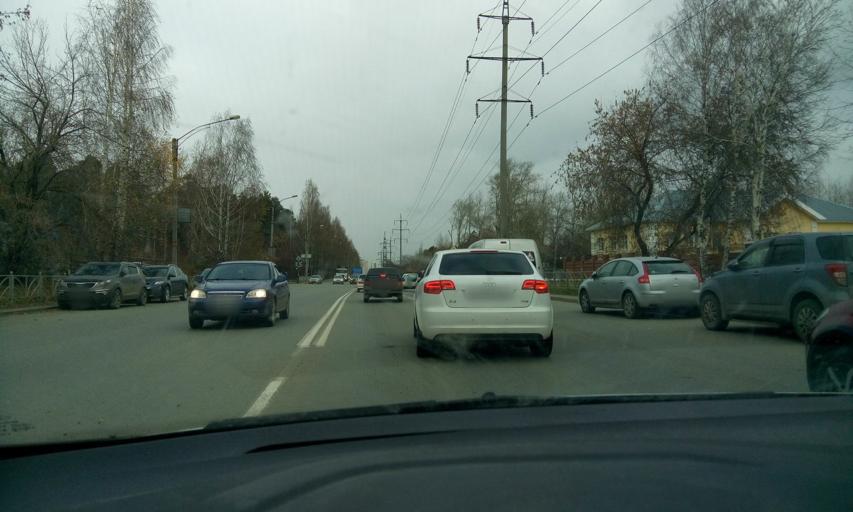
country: RU
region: Sverdlovsk
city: Sovkhoznyy
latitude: 56.7800
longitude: 60.5985
